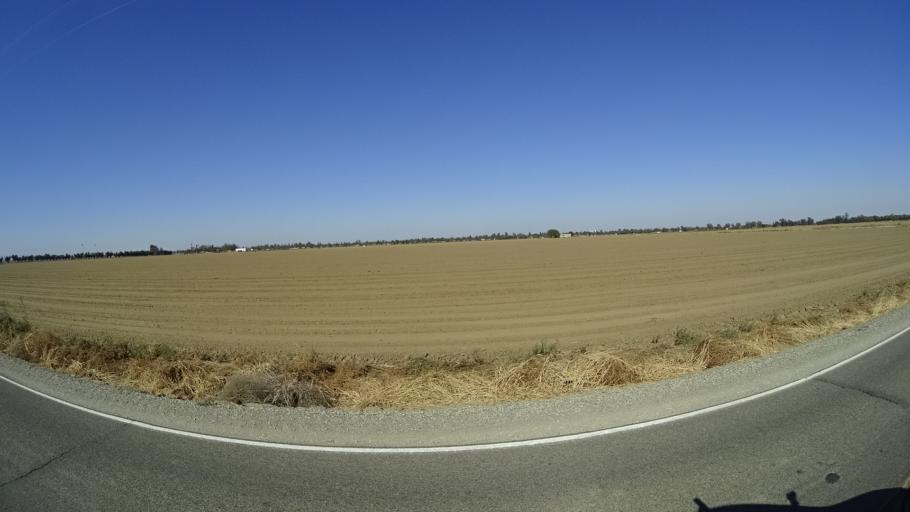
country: US
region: California
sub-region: Yolo County
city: Woodland
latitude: 38.6410
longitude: -121.7776
